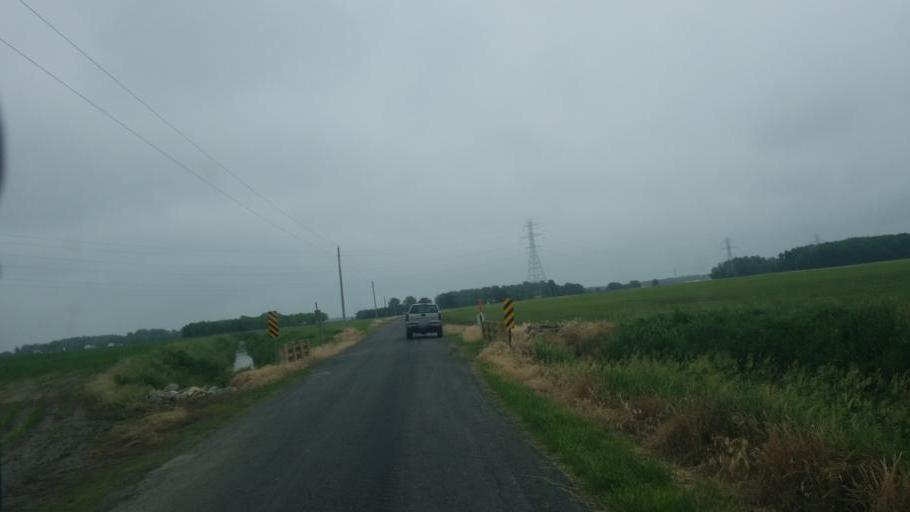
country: US
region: Indiana
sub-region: Marshall County
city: Bremen
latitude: 41.4793
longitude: -86.1319
